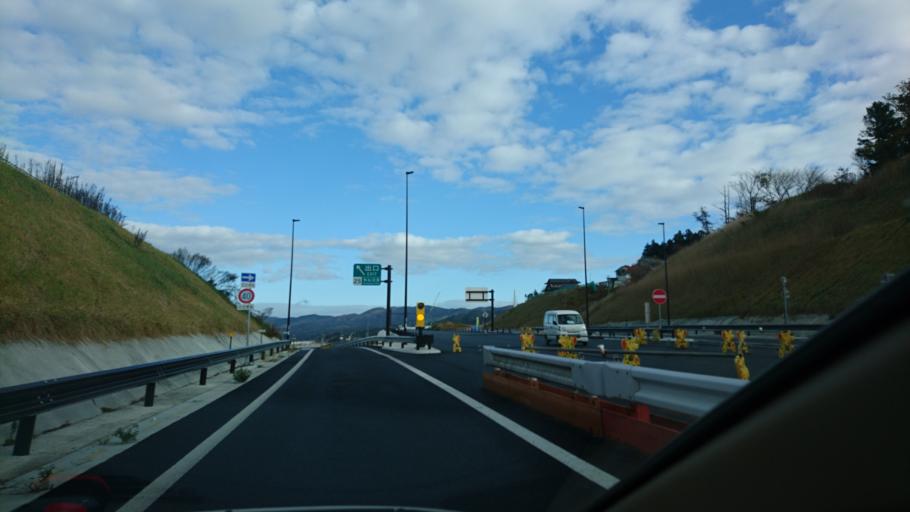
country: JP
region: Iwate
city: Ofunato
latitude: 38.8811
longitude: 141.5855
